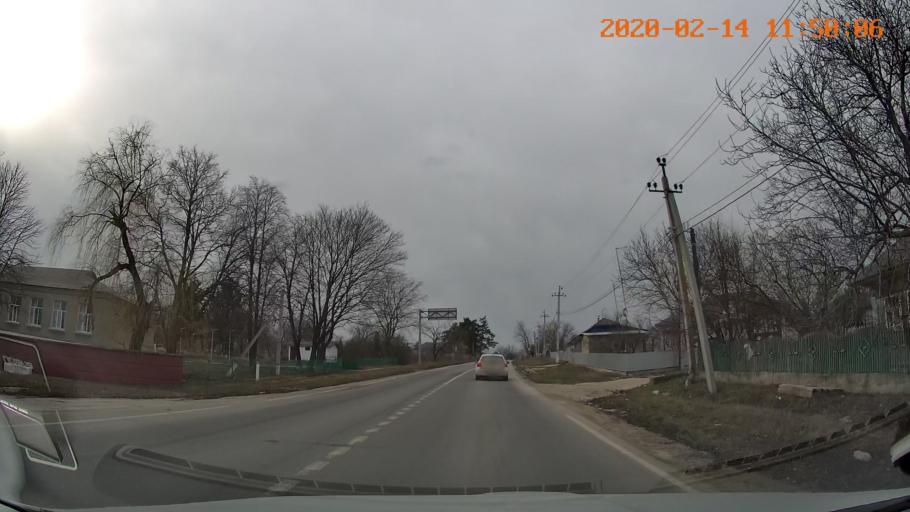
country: RO
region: Botosani
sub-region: Comuna Radauti-Prut
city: Miorcani
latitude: 48.2966
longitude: 26.9346
